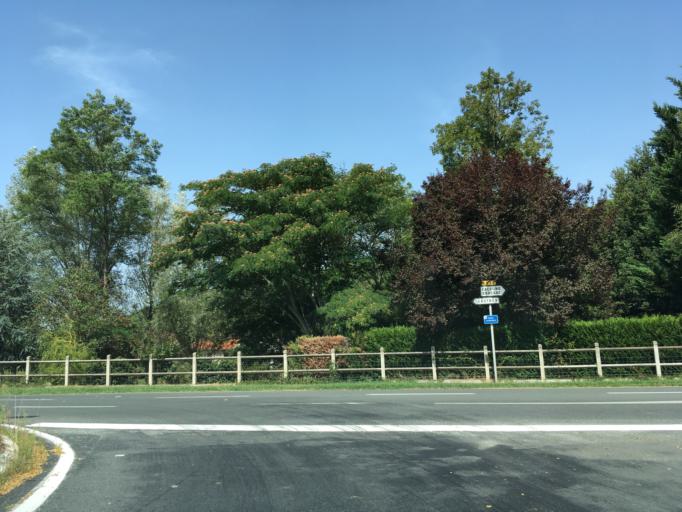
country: FR
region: Midi-Pyrenees
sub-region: Departement du Tarn
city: Burlats
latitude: 43.6210
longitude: 2.2875
